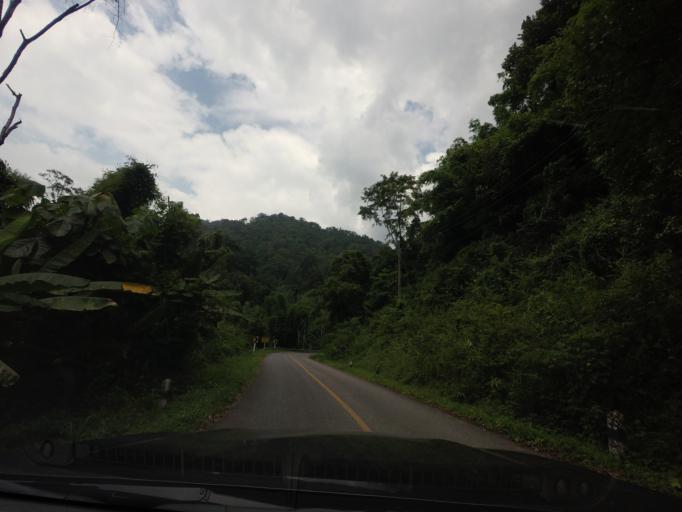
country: TH
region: Loei
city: Na Haeo
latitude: 17.7044
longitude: 100.9504
